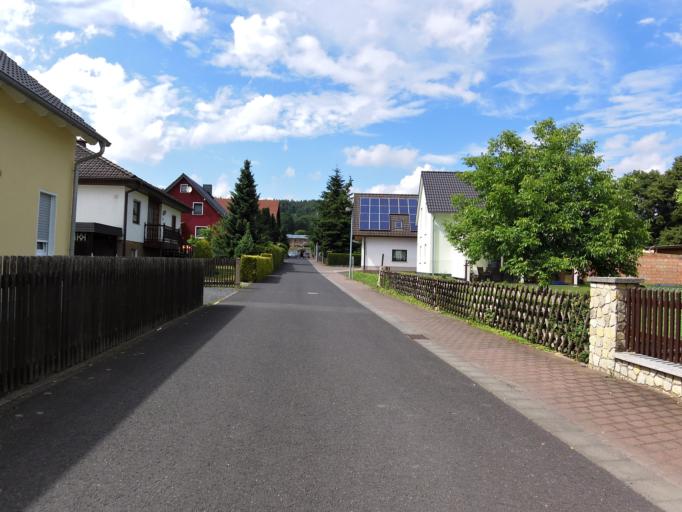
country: DE
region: Thuringia
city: Dorndorf
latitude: 50.8419
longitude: 10.1183
